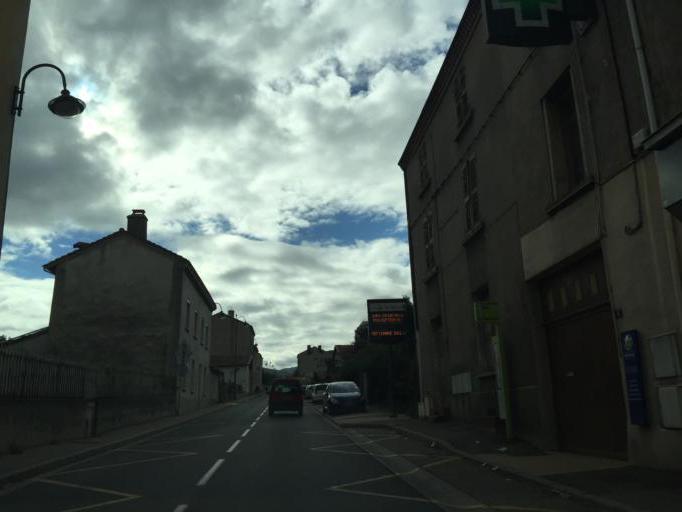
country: FR
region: Rhone-Alpes
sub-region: Departement de la Loire
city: La Grand-Croix
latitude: 45.4960
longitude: 4.5640
